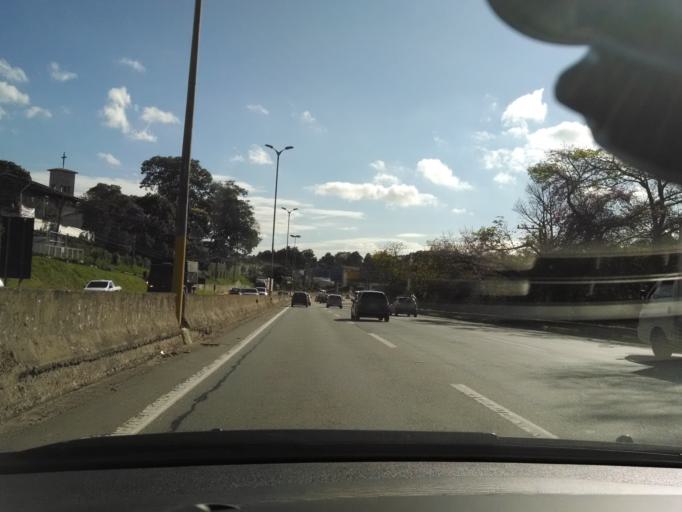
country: BR
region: Sao Paulo
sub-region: Embu
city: Embu
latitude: -23.5963
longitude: -46.8404
